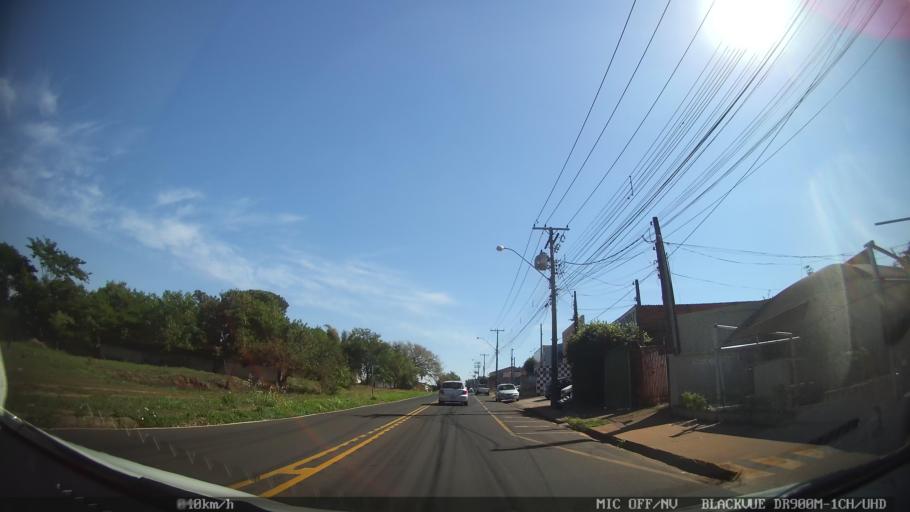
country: BR
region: Sao Paulo
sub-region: Sao Jose Do Rio Preto
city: Sao Jose do Rio Preto
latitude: -20.7767
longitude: -49.3831
